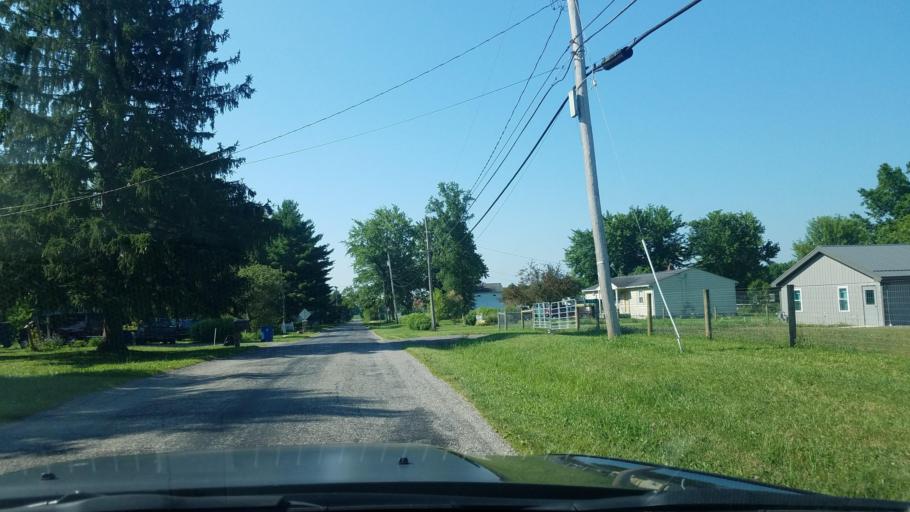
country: US
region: Ohio
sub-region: Trumbull County
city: Leavittsburg
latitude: 41.2788
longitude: -80.9254
